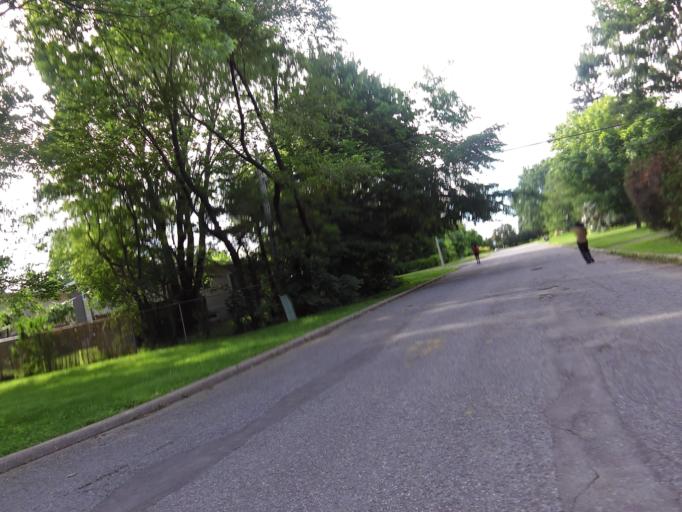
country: CA
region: Ontario
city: Bells Corners
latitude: 45.3479
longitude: -75.8008
